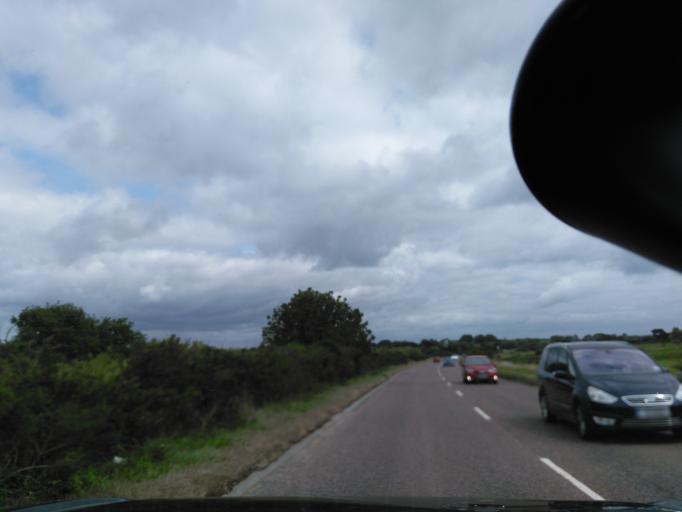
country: GB
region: England
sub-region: Dorset
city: Wareham
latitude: 50.6873
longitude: -2.1221
